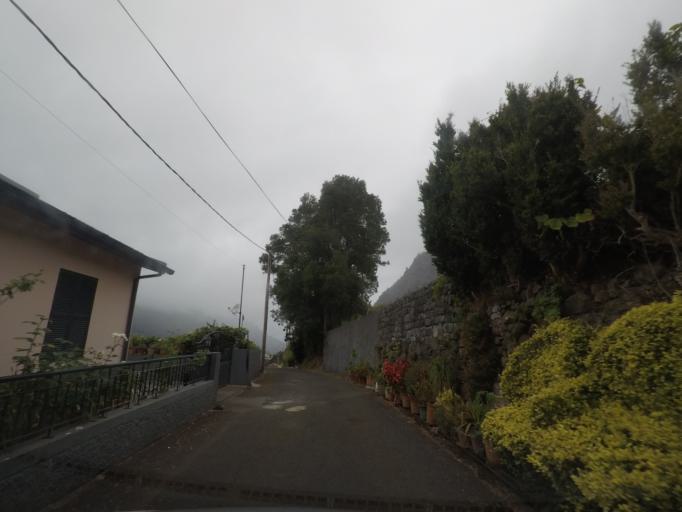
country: PT
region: Madeira
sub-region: Santana
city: Santana
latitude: 32.7691
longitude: -16.8433
